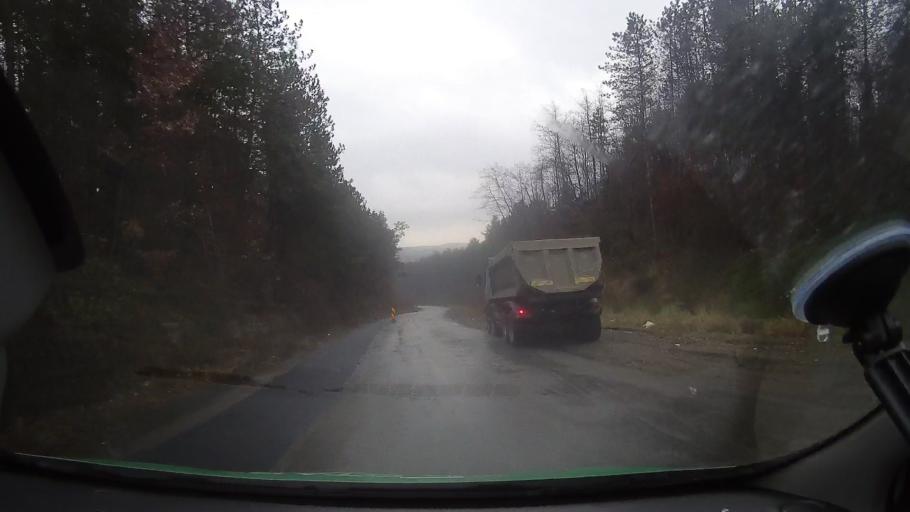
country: RO
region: Arad
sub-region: Comuna Halmagiu
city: Halmagiu
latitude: 46.2799
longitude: 22.5885
